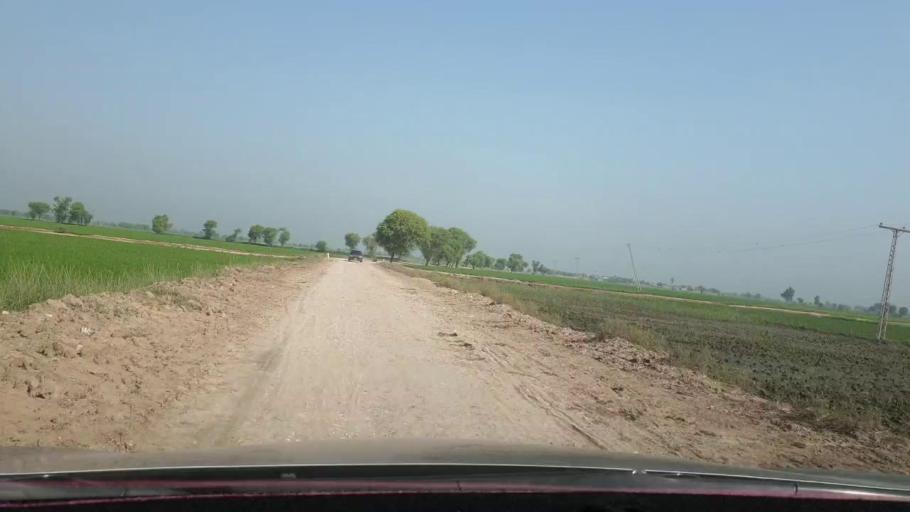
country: PK
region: Sindh
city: Kambar
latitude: 27.5924
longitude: 67.9379
